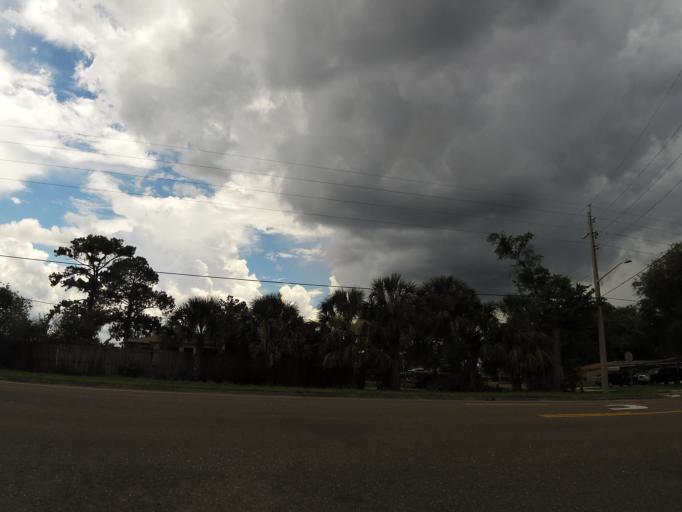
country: US
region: Florida
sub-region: Duval County
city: Jacksonville
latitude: 30.4199
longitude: -81.6695
